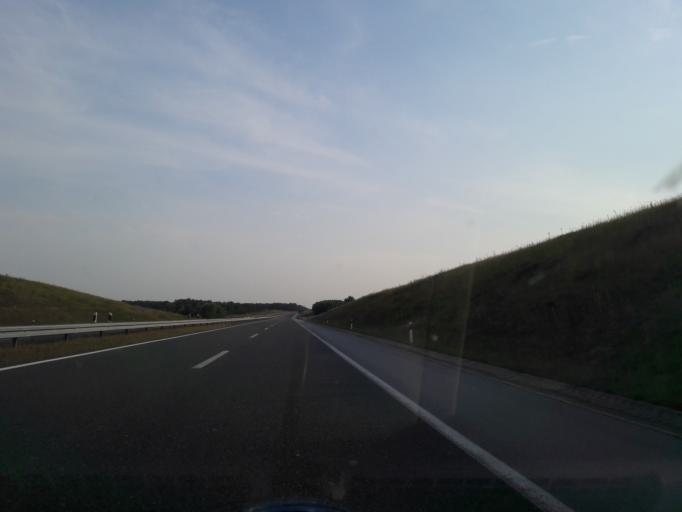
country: HR
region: Osjecko-Baranjska
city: Piskorevci
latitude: 45.2956
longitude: 18.3601
